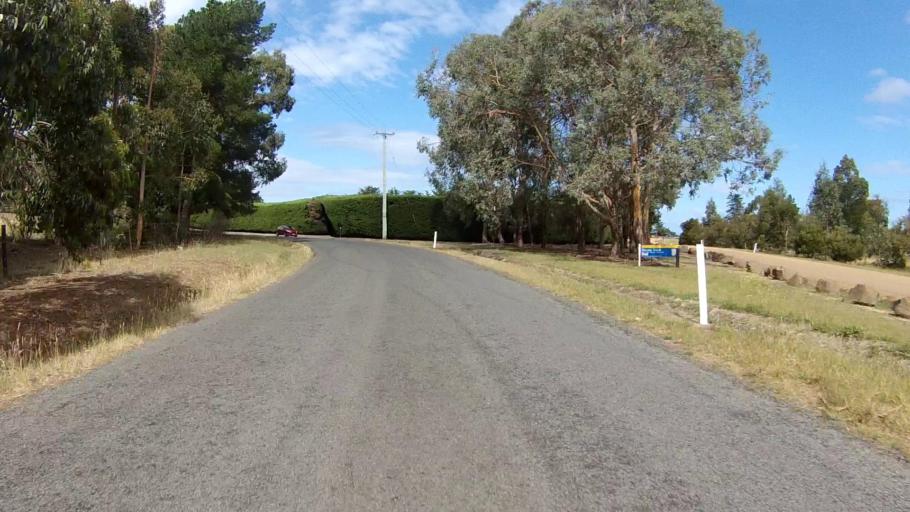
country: AU
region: Tasmania
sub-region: Clarence
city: Acton Park
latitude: -42.8886
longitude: 147.4990
